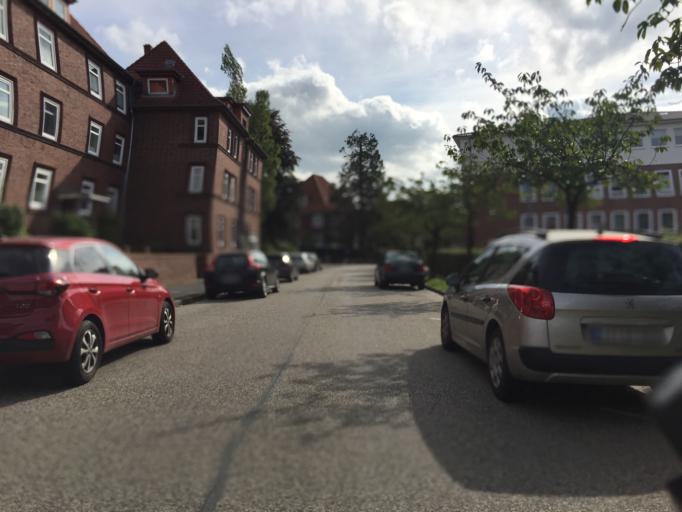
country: DE
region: Schleswig-Holstein
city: Itzehoe
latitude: 53.9293
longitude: 9.5144
